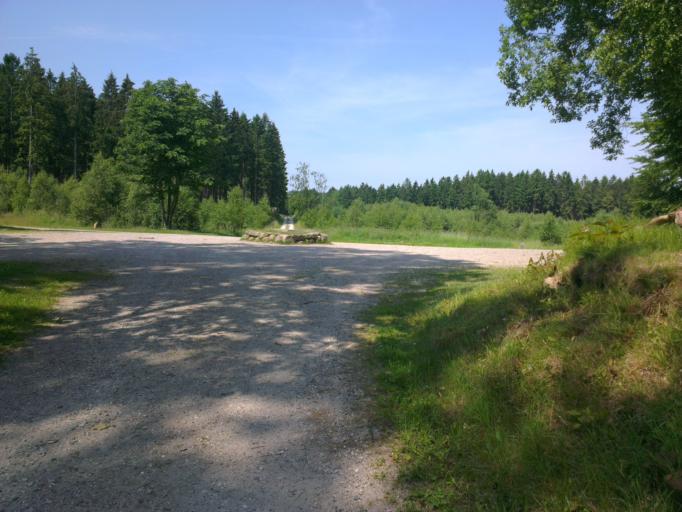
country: DK
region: Capital Region
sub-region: Allerod Kommune
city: Lillerod
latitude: 55.9127
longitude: 12.3586
